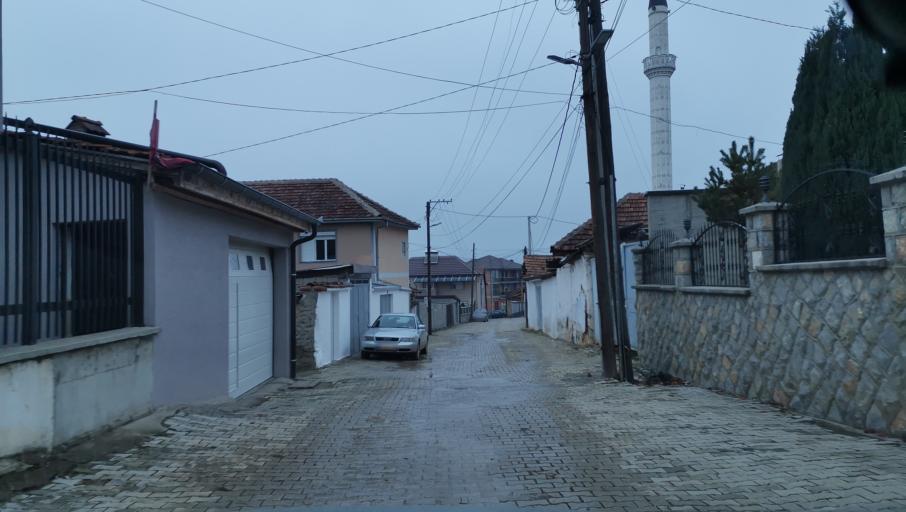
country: MK
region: Debar
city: Debar
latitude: 41.5278
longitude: 20.5242
